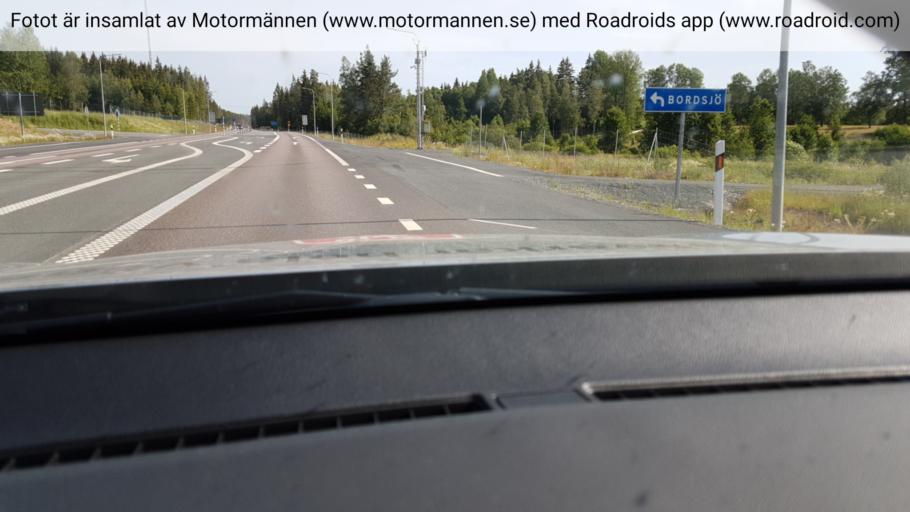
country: SE
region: Joenkoeping
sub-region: Aneby Kommun
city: Aneby
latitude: 57.8482
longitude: 14.8667
